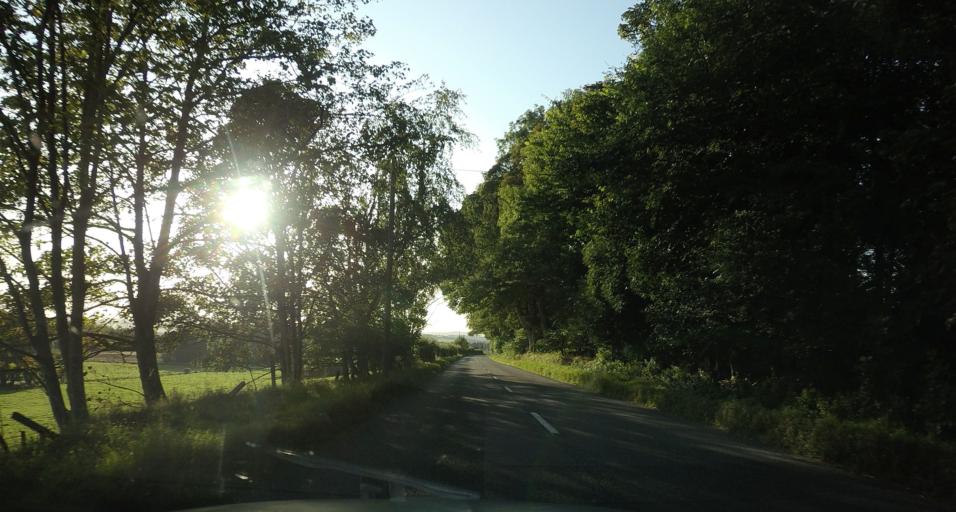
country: GB
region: Scotland
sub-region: Aberdeenshire
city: Westhill
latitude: 57.1553
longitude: -2.3250
